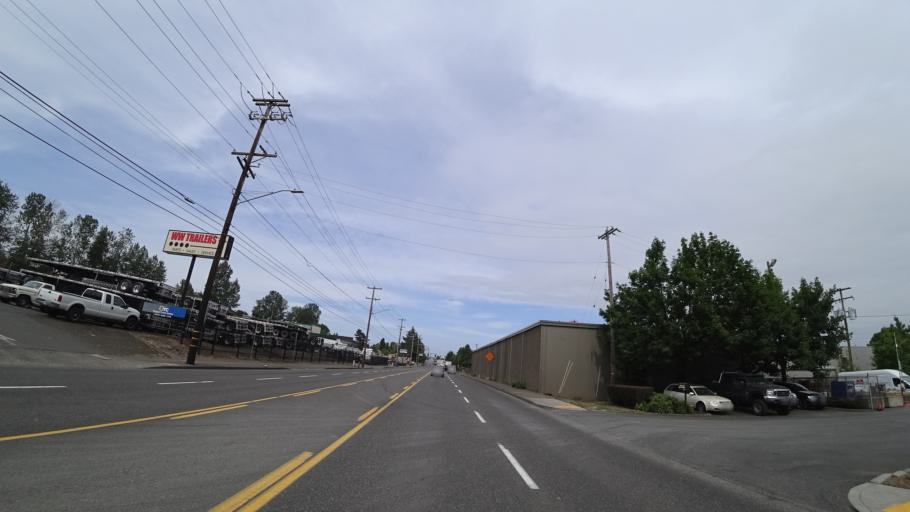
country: US
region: Oregon
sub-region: Multnomah County
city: Portland
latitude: 45.5703
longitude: -122.6111
